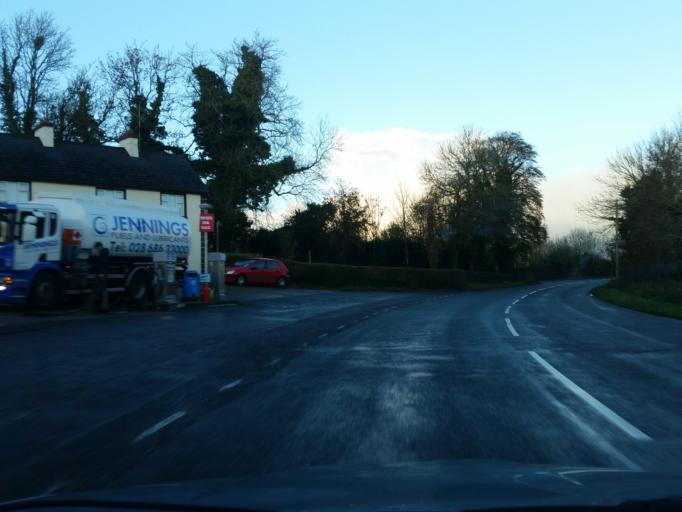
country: GB
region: Northern Ireland
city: Lisnaskea
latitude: 54.2037
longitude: -7.4926
